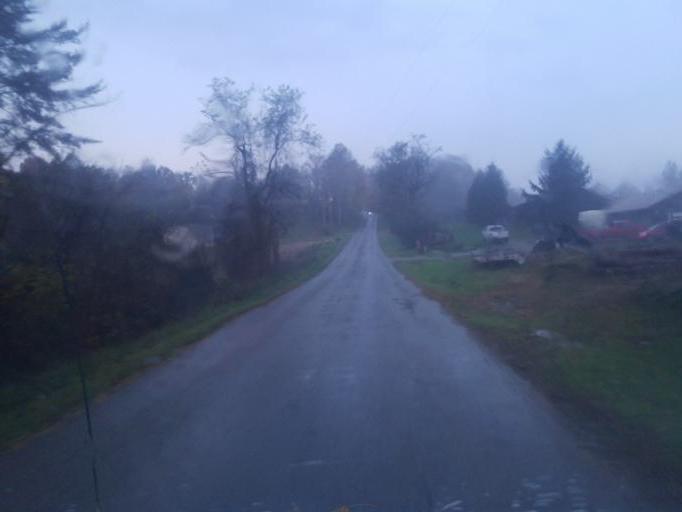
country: US
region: Ohio
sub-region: Morgan County
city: McConnelsville
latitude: 39.5235
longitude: -81.8442
